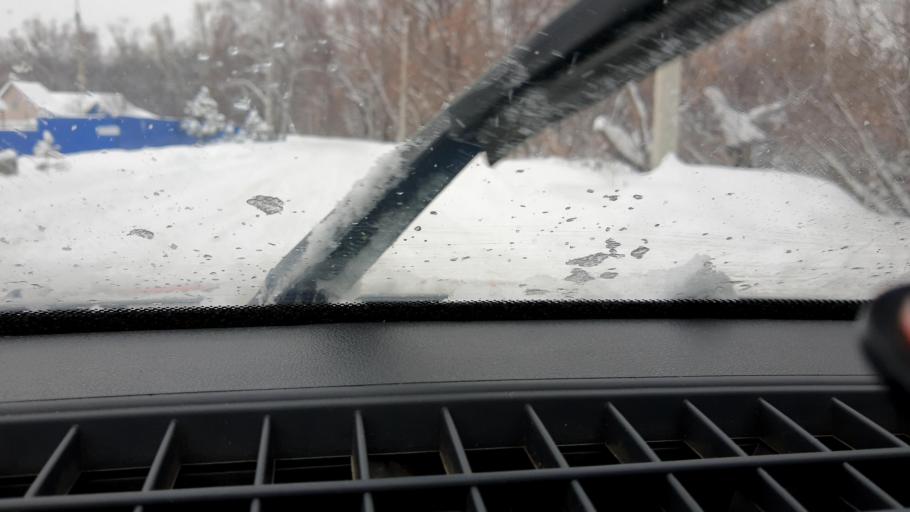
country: RU
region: Bashkortostan
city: Mikhaylovka
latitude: 54.8037
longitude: 55.8726
